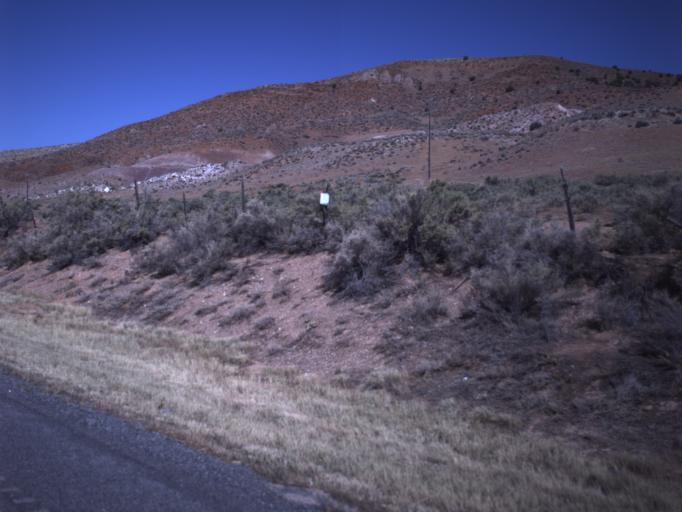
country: US
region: Utah
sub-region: Sanpete County
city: Gunnison
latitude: 39.1638
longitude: -111.7360
